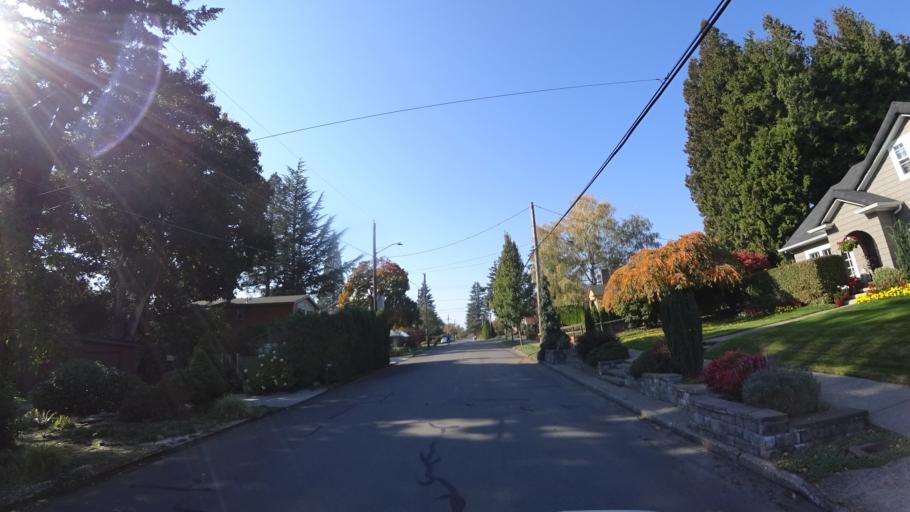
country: US
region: Oregon
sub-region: Multnomah County
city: Gresham
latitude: 45.4988
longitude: -122.4440
